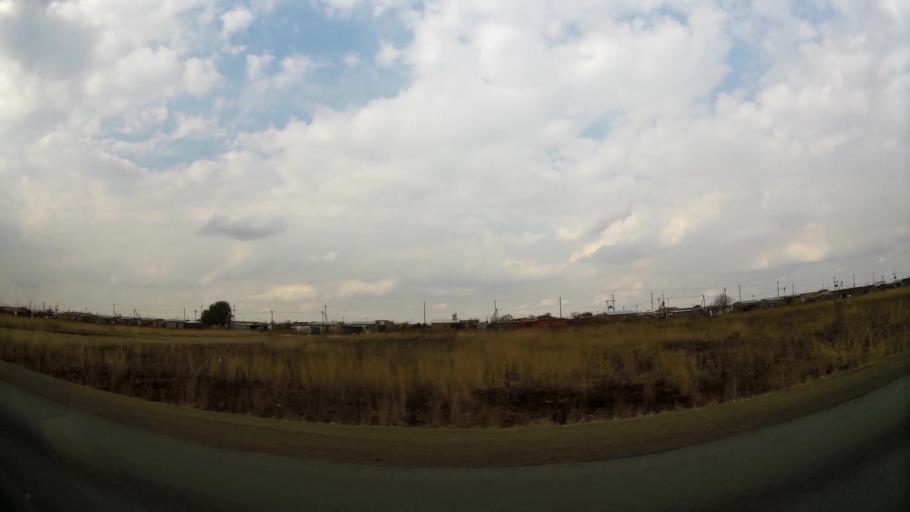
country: ZA
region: Orange Free State
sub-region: Fezile Dabi District Municipality
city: Sasolburg
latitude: -26.8607
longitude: 27.8882
